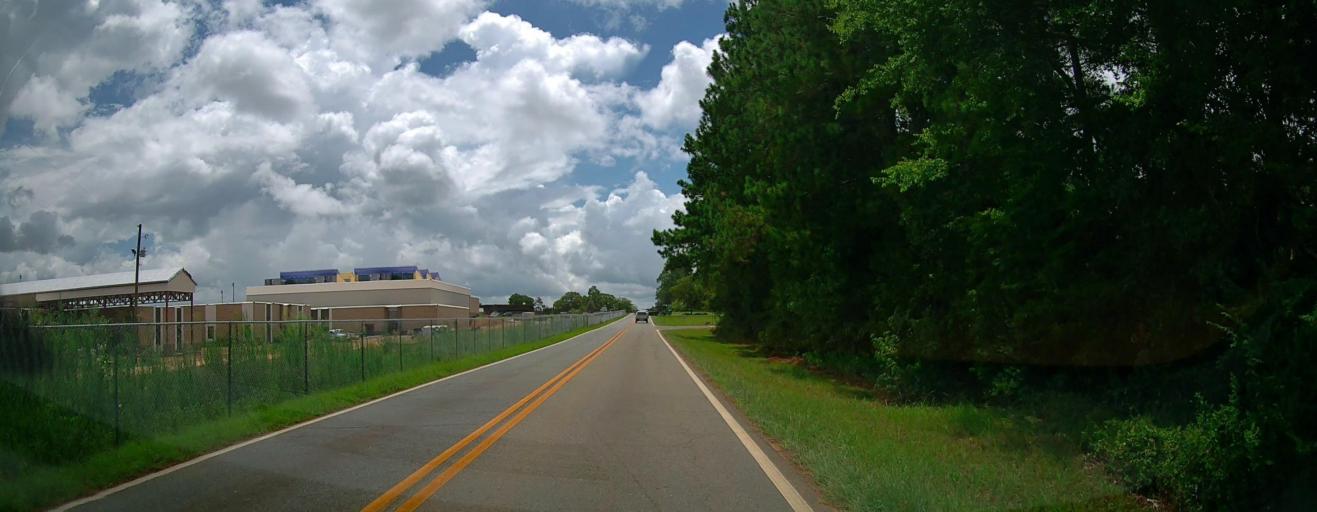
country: US
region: Georgia
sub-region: Pulaski County
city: Hawkinsville
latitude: 32.2851
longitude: -83.4920
